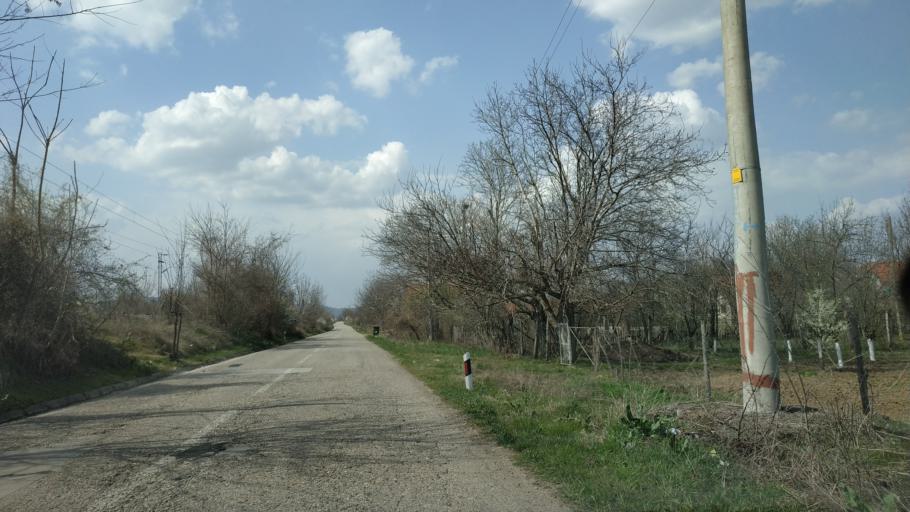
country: RS
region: Central Serbia
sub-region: Nisavski Okrug
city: Razanj
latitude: 43.5674
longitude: 21.5914
